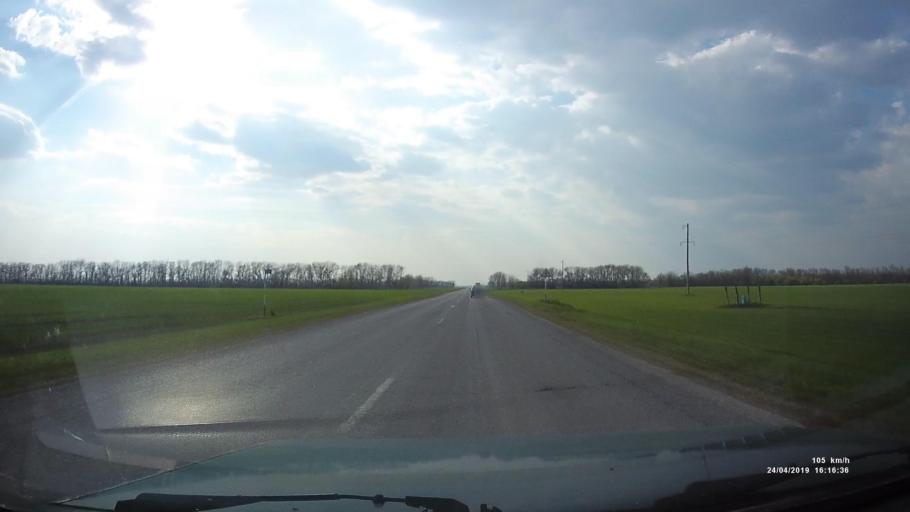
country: RU
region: Rostov
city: Sovetskoye
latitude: 46.7649
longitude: 42.1543
